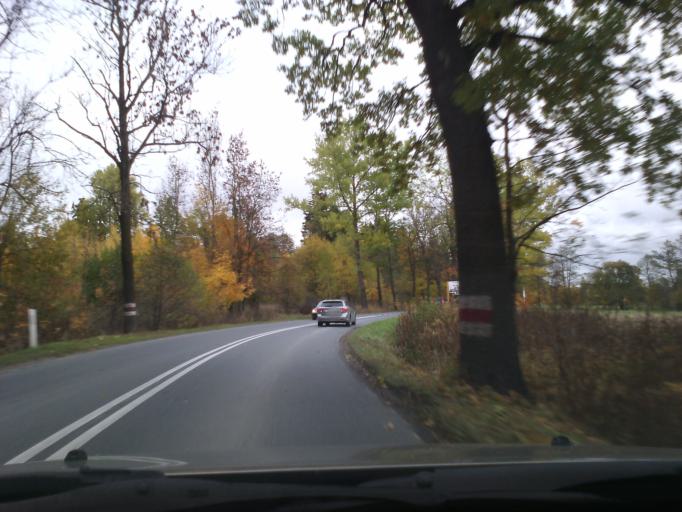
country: PL
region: Lower Silesian Voivodeship
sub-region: Powiat kamiennogorski
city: Kamienna Gora
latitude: 50.7755
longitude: 15.9403
